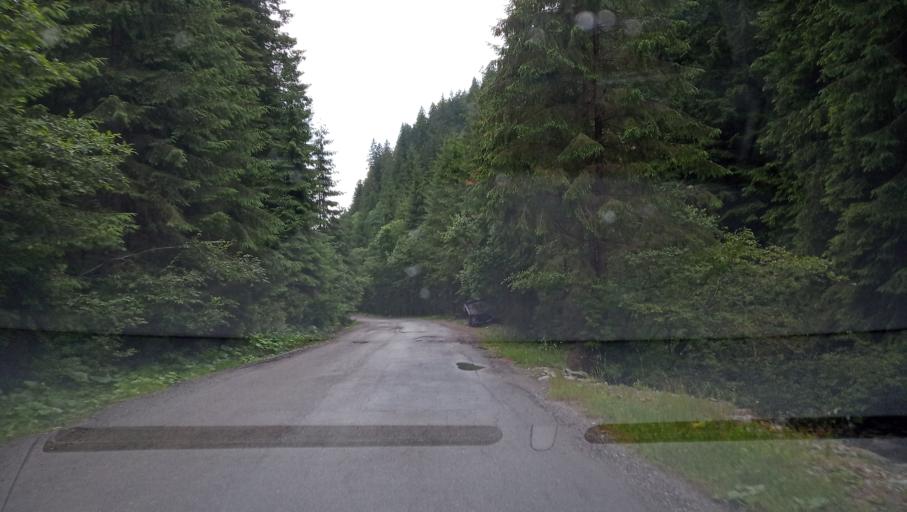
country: RO
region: Hunedoara
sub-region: Oras Petrila
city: Petrila
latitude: 45.4081
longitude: 23.5237
